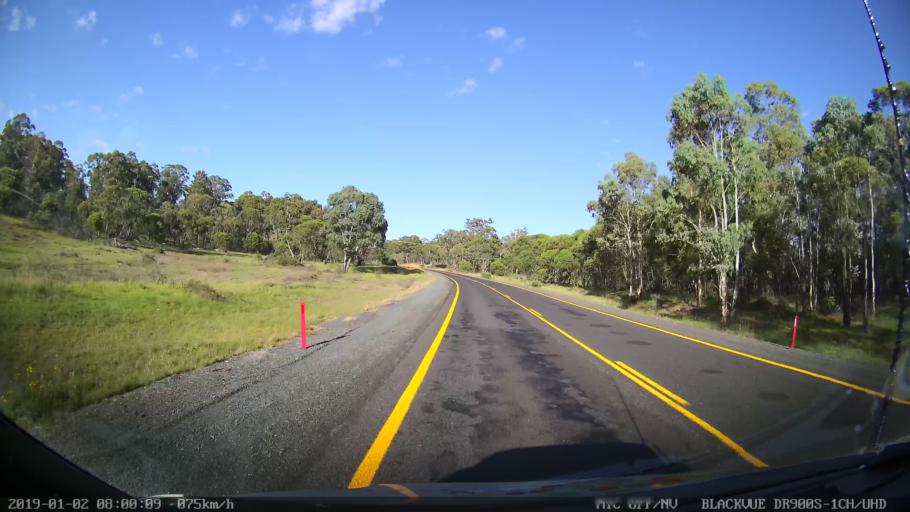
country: AU
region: New South Wales
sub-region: Tumut Shire
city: Tumut
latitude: -35.6439
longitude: 148.4492
